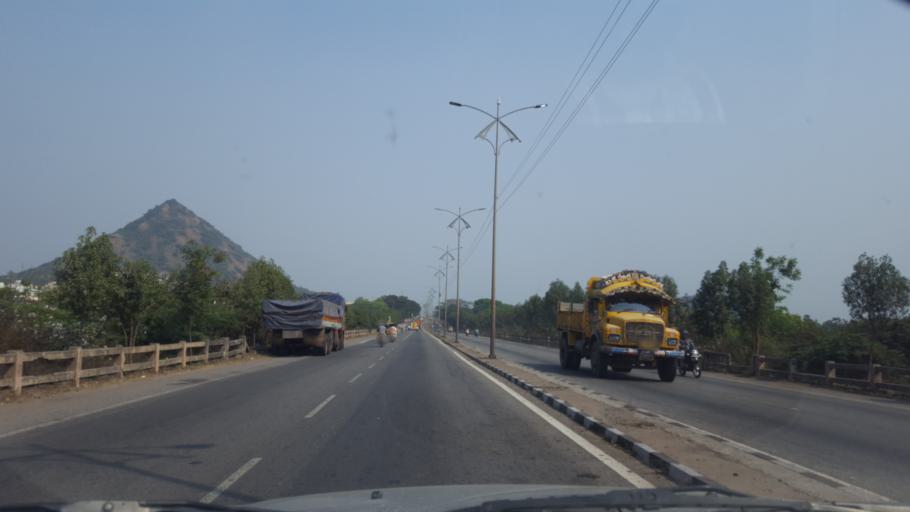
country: IN
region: Andhra Pradesh
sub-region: Vishakhapatnam
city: Visakhapatnam
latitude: 17.6887
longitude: 83.1192
